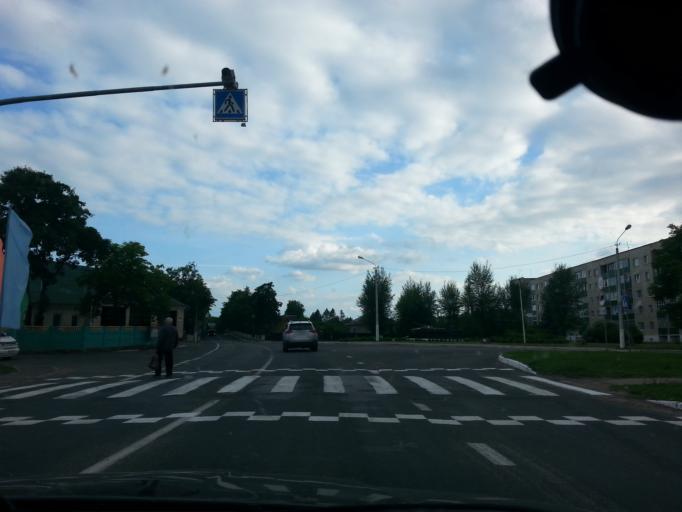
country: BY
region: Minsk
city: Myadzyel
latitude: 54.8678
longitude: 26.9343
